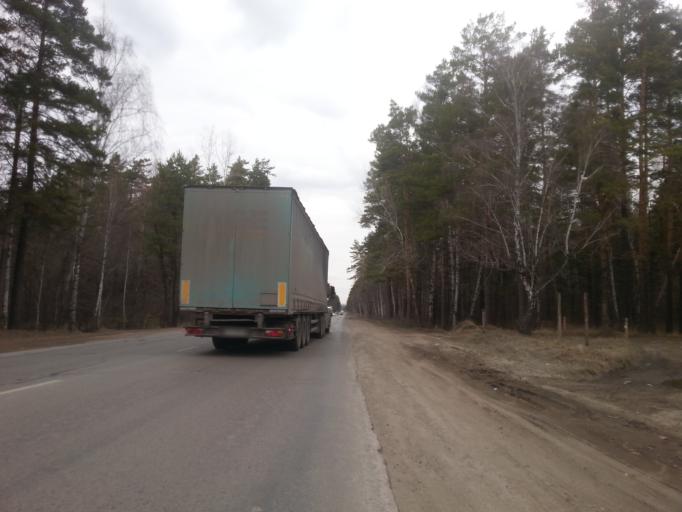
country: RU
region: Altai Krai
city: Yuzhnyy
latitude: 53.2748
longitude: 83.7214
